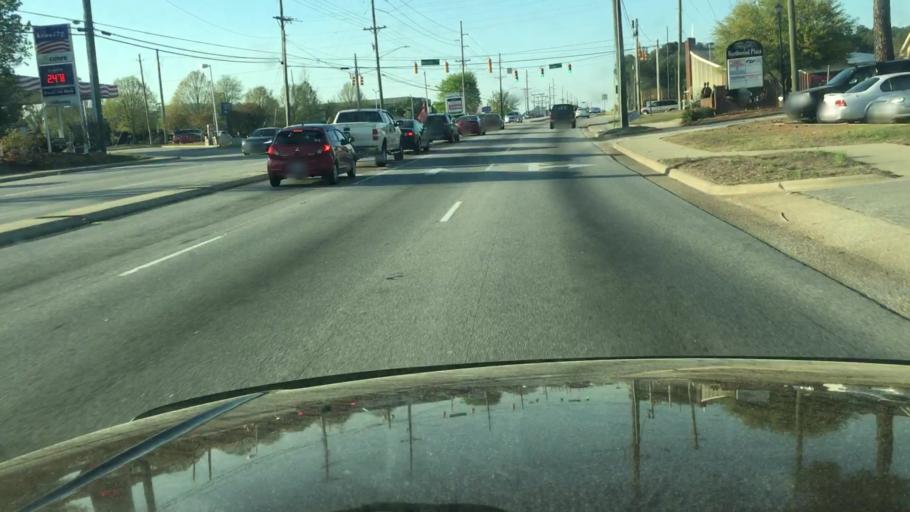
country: US
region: North Carolina
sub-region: Cumberland County
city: Fayetteville
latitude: 35.1161
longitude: -78.8799
